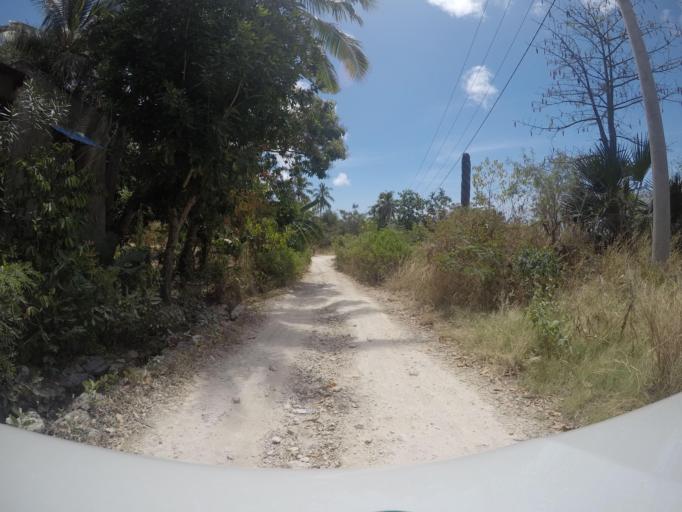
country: TL
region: Baucau
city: Baucau
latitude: -8.4537
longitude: 126.4415
